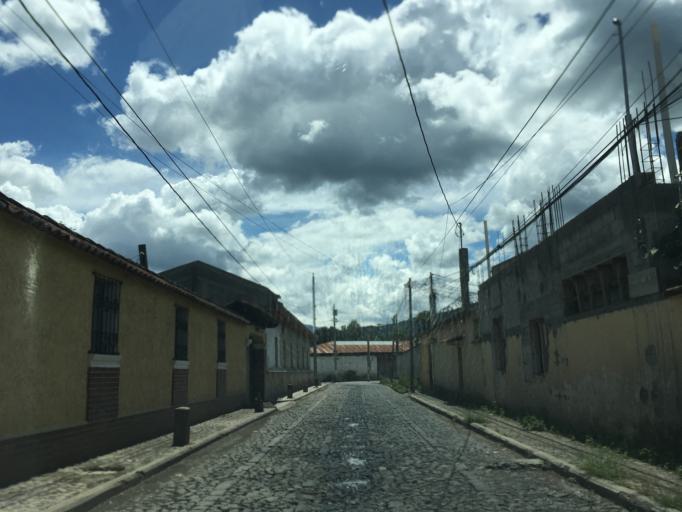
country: GT
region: Sacatepequez
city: Antigua Guatemala
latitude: 14.5455
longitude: -90.7324
